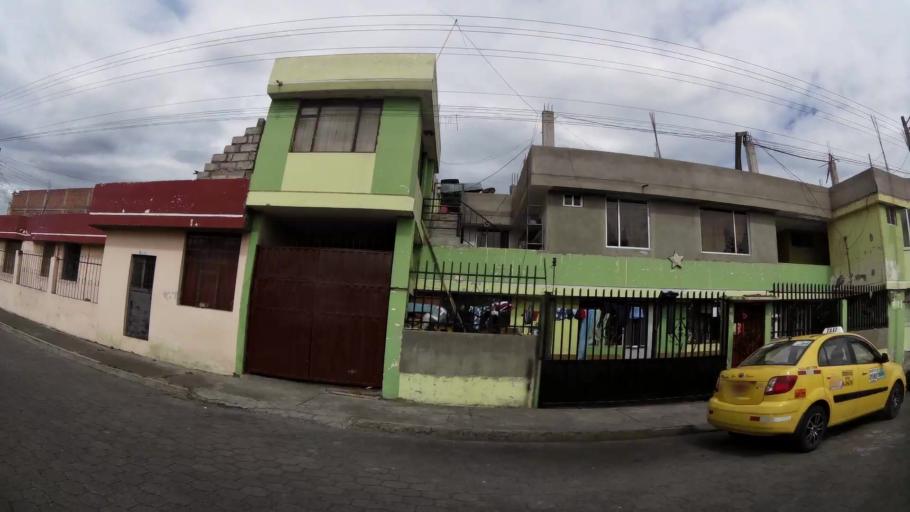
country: EC
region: Cotopaxi
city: Latacunga
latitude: -0.9235
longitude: -78.6236
